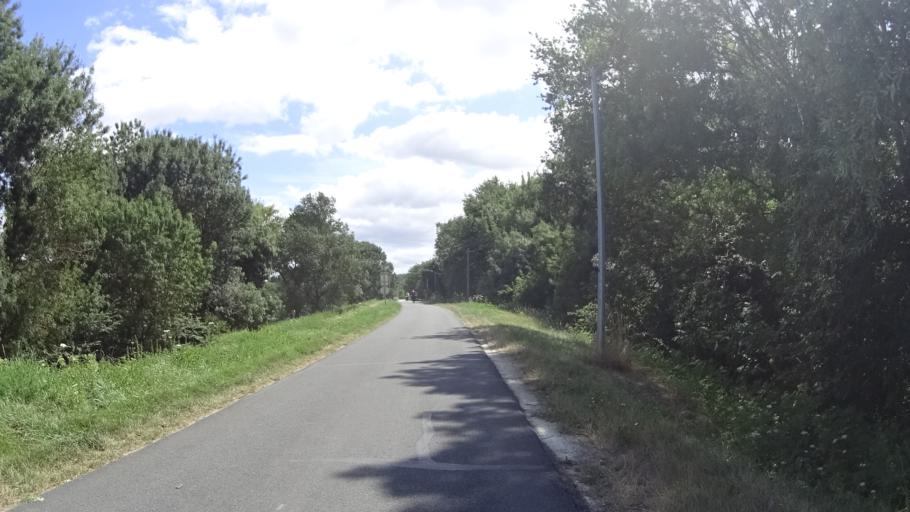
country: FR
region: Centre
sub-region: Departement d'Indre-et-Loire
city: Villandry
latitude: 47.3442
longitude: 0.5088
